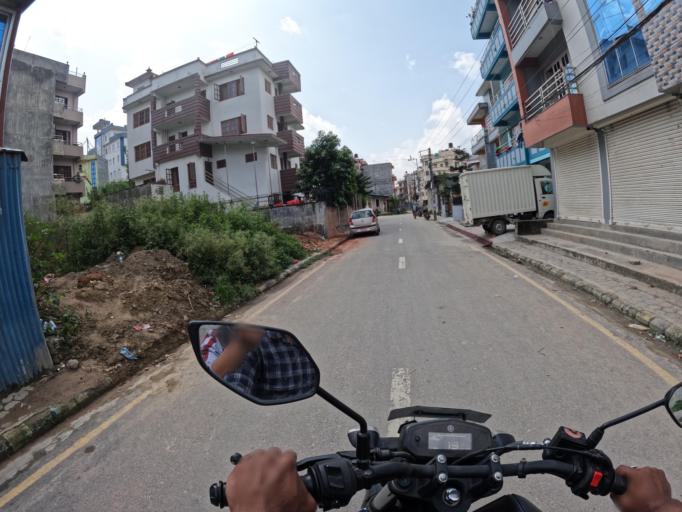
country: NP
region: Central Region
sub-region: Bagmati Zone
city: Patan
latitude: 27.6711
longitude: 85.3563
